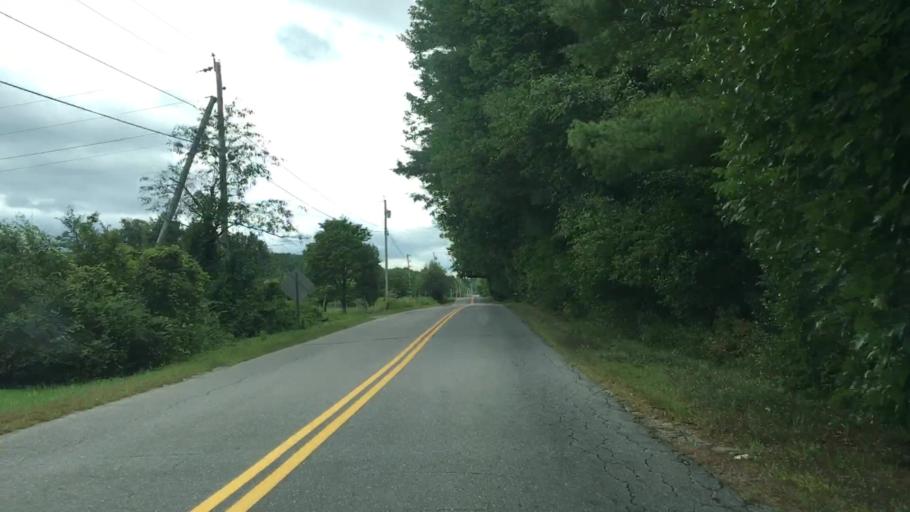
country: US
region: Maine
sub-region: Kennebec County
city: Hallowell
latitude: 44.2744
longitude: -69.8113
